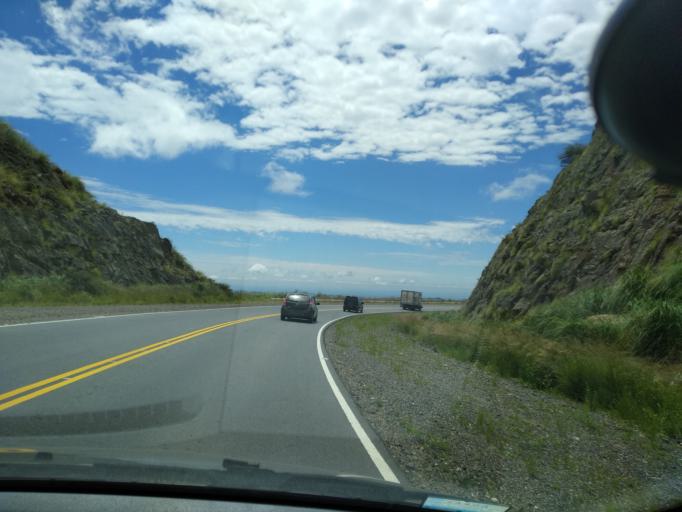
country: AR
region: Cordoba
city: Cuesta Blanca
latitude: -31.6014
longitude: -64.6979
